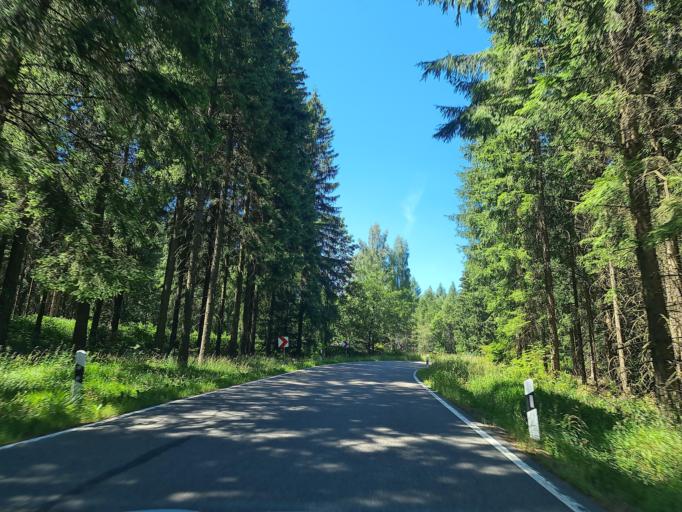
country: DE
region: Saxony
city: Rechenberg-Bienenmuhle
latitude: 50.7157
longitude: 13.5325
